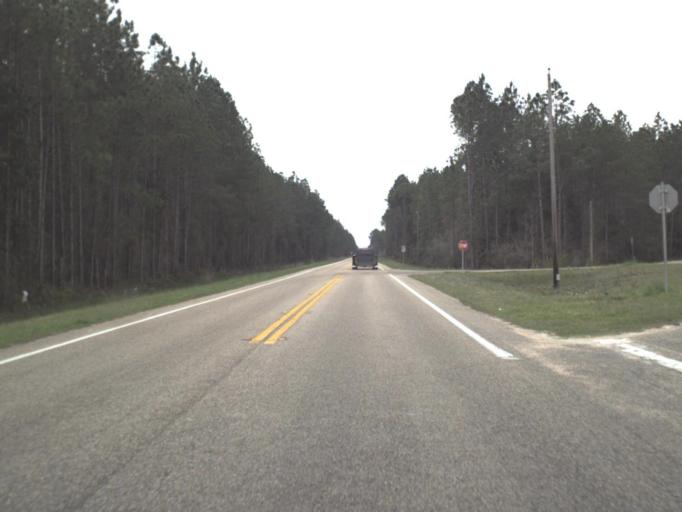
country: US
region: Florida
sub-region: Gulf County
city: Port Saint Joe
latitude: 29.8553
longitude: -85.2515
